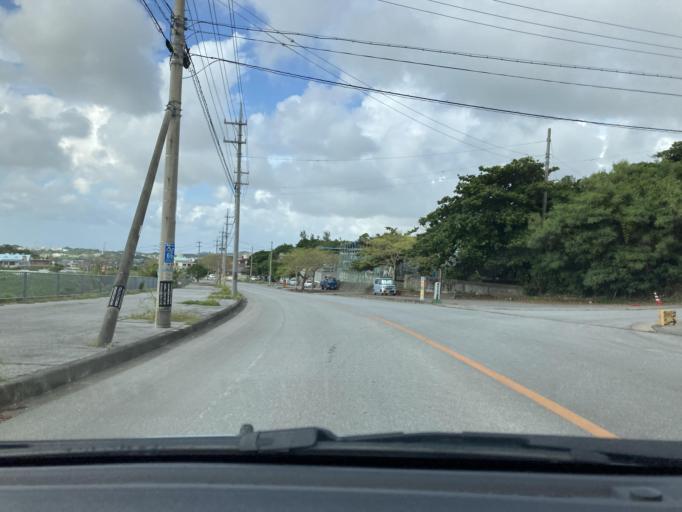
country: JP
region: Okinawa
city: Itoman
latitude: 26.1229
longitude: 127.6934
